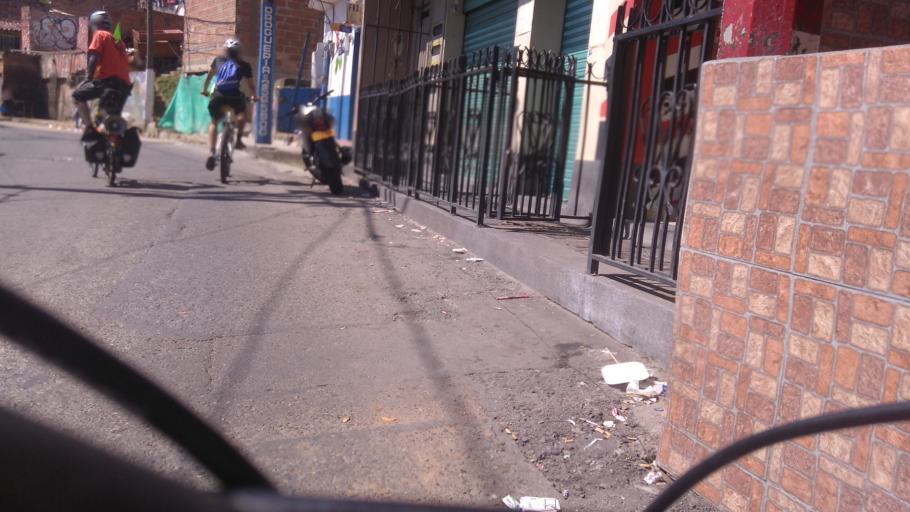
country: CO
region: Antioquia
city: Itagui
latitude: 6.2265
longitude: -75.6059
